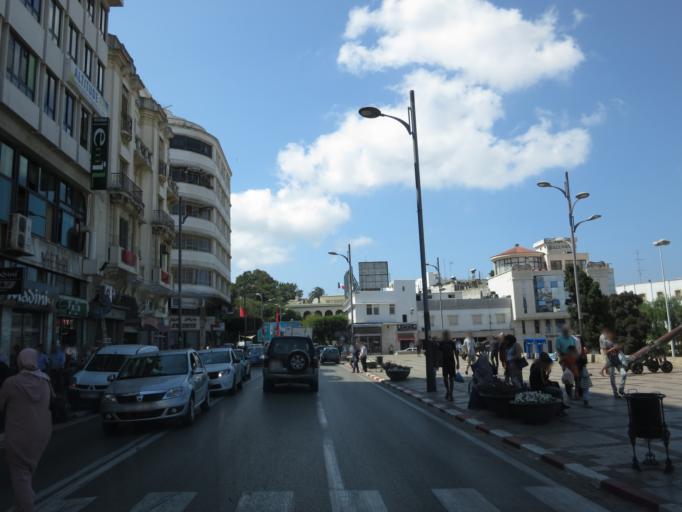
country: MA
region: Tanger-Tetouan
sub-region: Tanger-Assilah
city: Tangier
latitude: 35.7807
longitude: -5.8115
